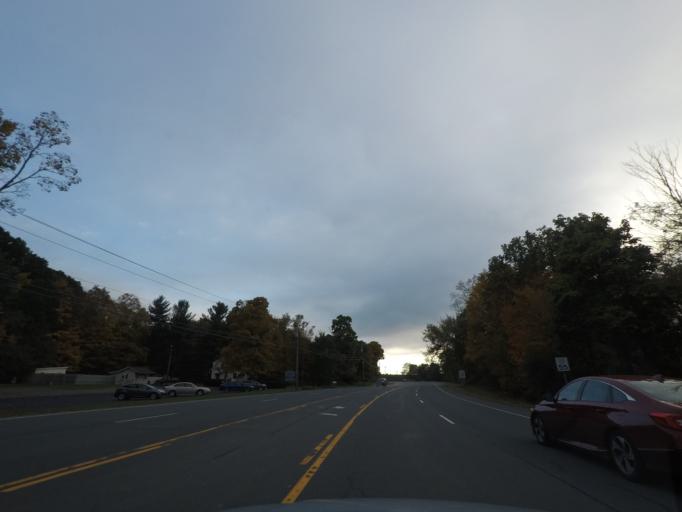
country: US
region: New York
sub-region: Rensselaer County
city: East Greenbush
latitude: 42.5459
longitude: -73.6724
